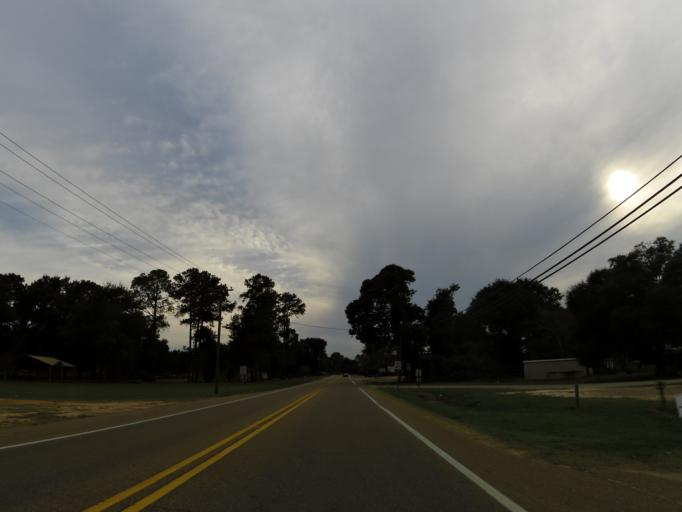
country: US
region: Alabama
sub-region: Monroe County
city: Frisco City
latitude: 31.4288
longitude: -87.4053
